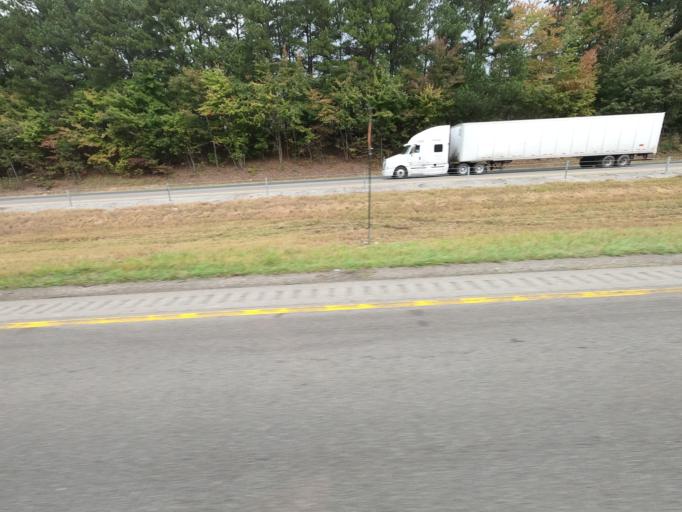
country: US
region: Tennessee
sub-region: Dickson County
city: Burns
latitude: 36.0189
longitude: -87.3406
